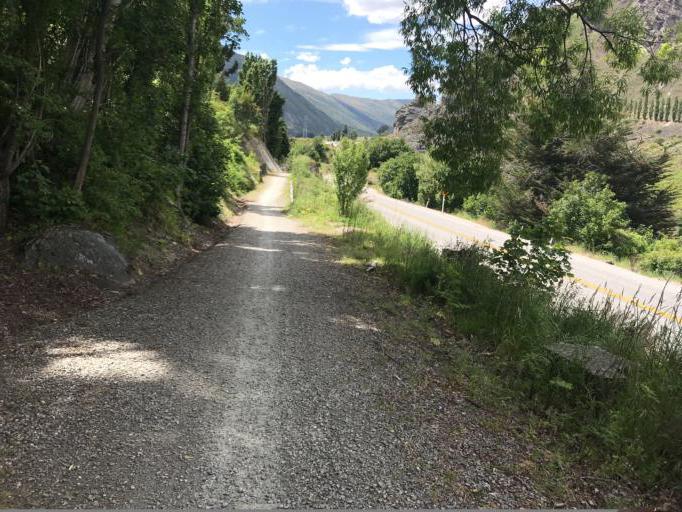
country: NZ
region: Otago
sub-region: Queenstown-Lakes District
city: Arrowtown
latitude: -45.0095
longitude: 168.8927
